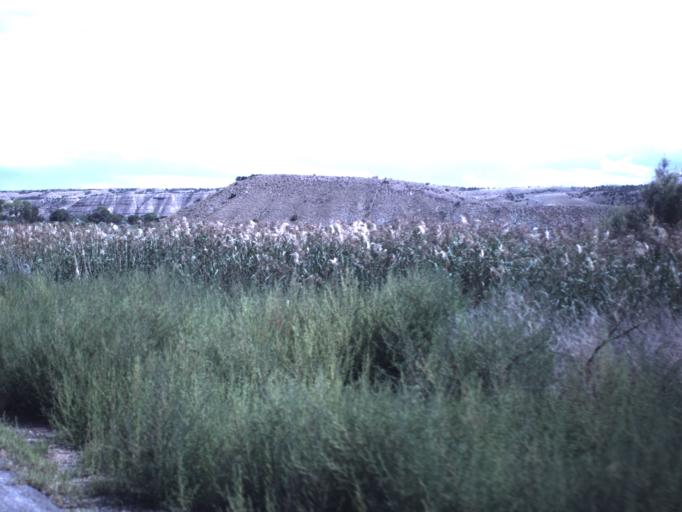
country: US
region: Utah
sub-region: Duchesne County
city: Duchesne
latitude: 40.1728
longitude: -110.4254
